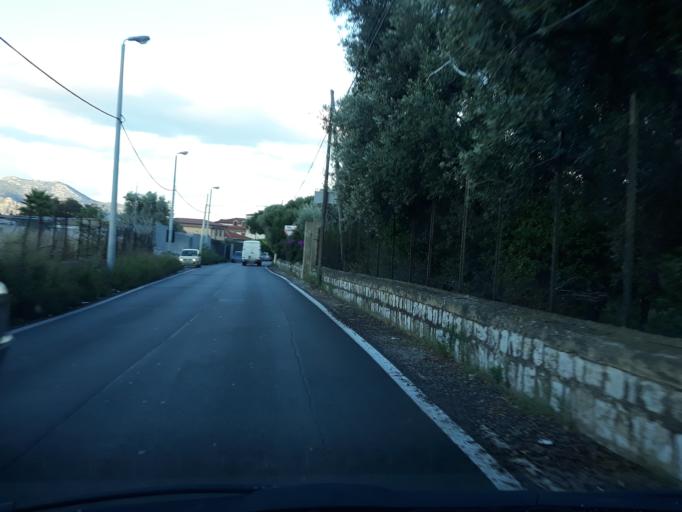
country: IT
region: Sicily
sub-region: Palermo
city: Villa Ciambra
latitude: 38.0854
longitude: 13.3268
